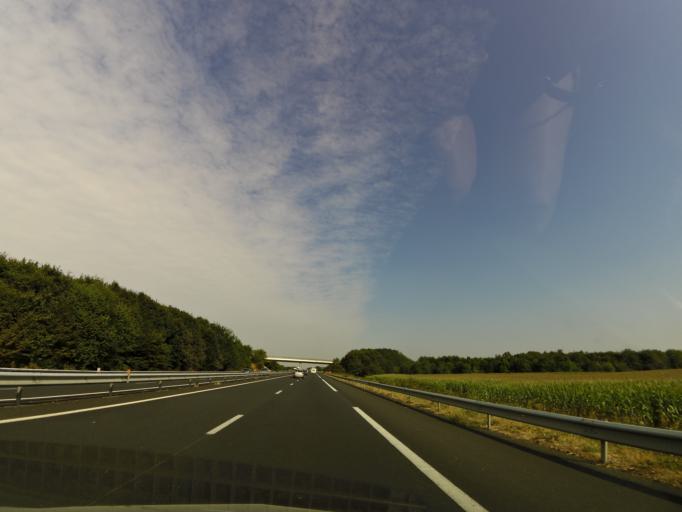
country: FR
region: Pays de la Loire
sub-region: Departement de la Vendee
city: Bouffere
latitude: 46.9304
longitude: -1.3382
